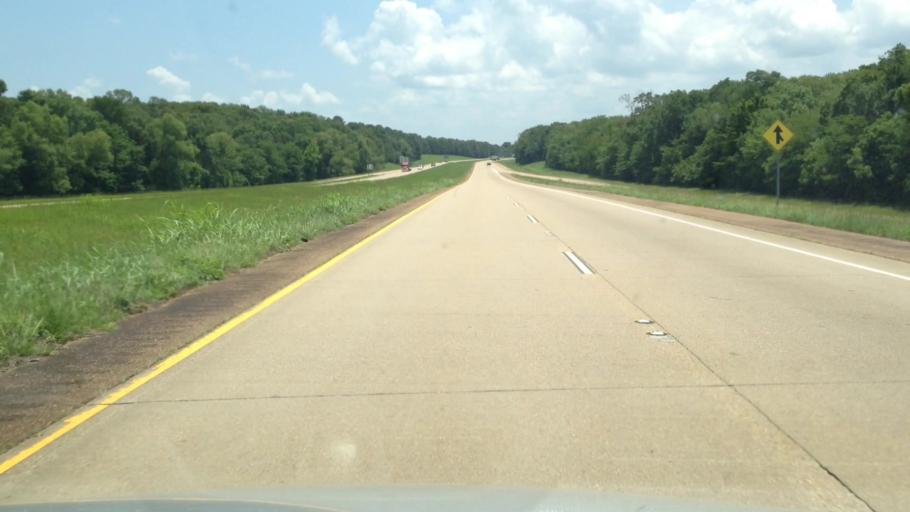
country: US
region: Louisiana
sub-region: Rapides Parish
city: Woodworth
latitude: 31.1620
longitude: -92.4585
